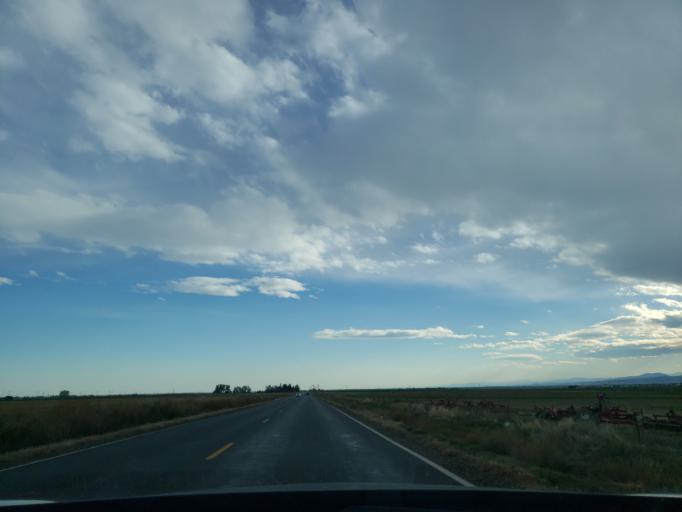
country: US
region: Colorado
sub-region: Larimer County
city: Wellington
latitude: 40.6304
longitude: -105.0197
